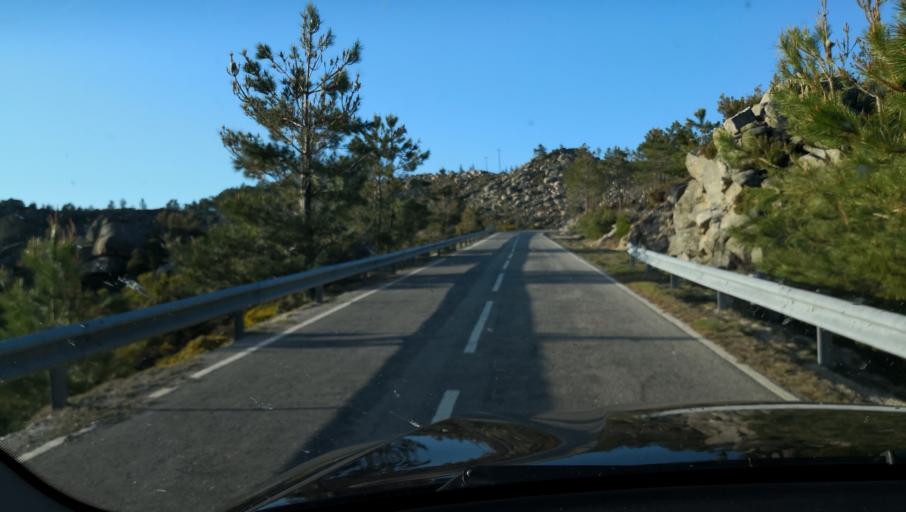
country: PT
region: Vila Real
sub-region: Vila Real
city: Vila Real
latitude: 41.3361
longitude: -7.7899
